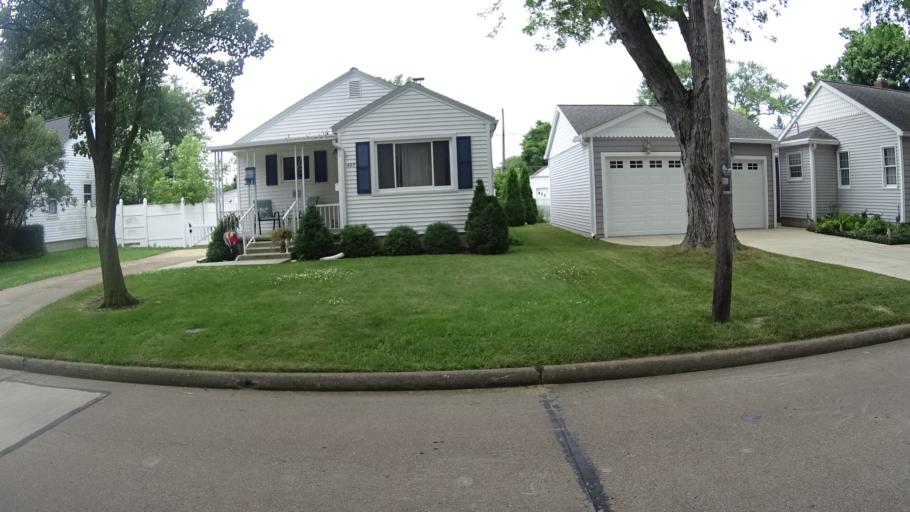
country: US
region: Ohio
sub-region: Erie County
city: Huron
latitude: 41.3894
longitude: -82.5393
